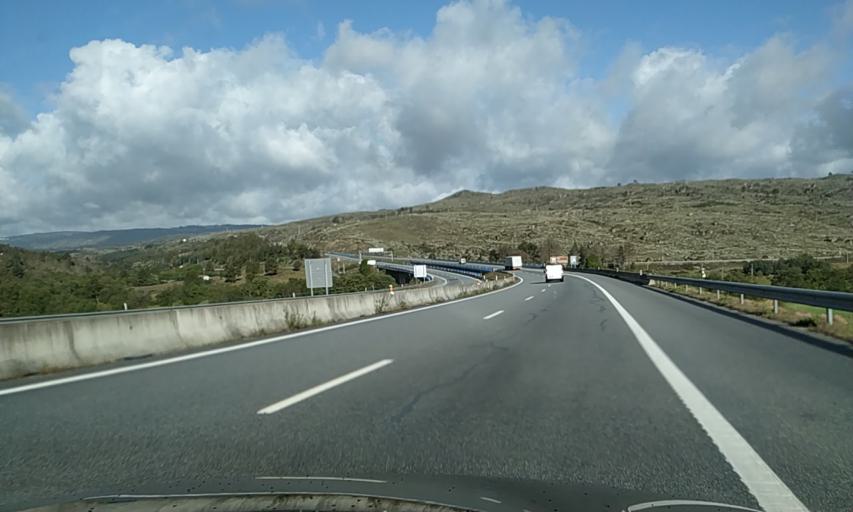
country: PT
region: Guarda
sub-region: Celorico da Beira
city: Celorico da Beira
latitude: 40.6306
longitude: -7.4304
